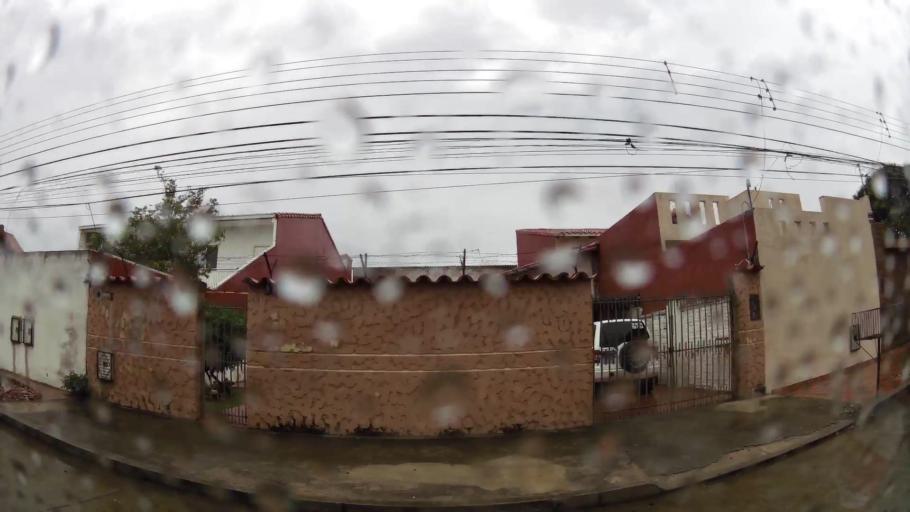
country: BO
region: Santa Cruz
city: Santa Cruz de la Sierra
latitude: -17.7719
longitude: -63.1497
